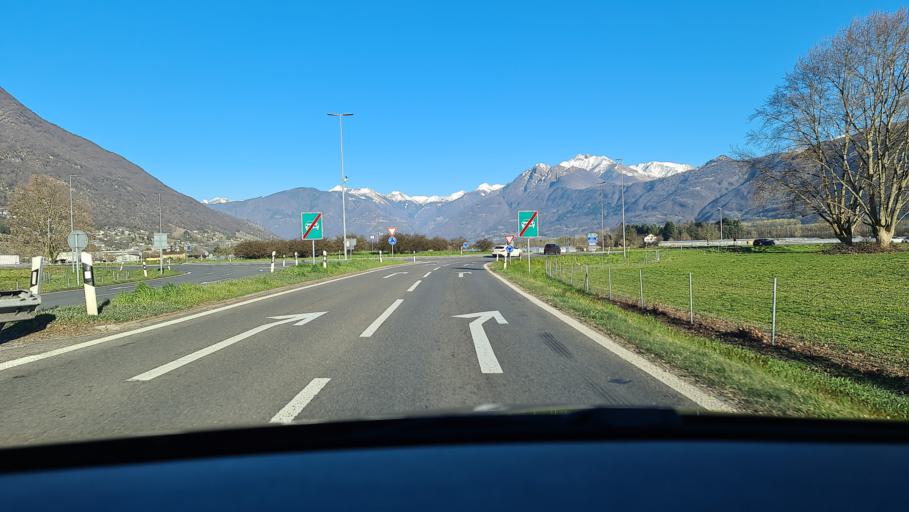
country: CH
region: Ticino
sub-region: Locarno District
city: Gordola
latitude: 46.1682
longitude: 8.8839
